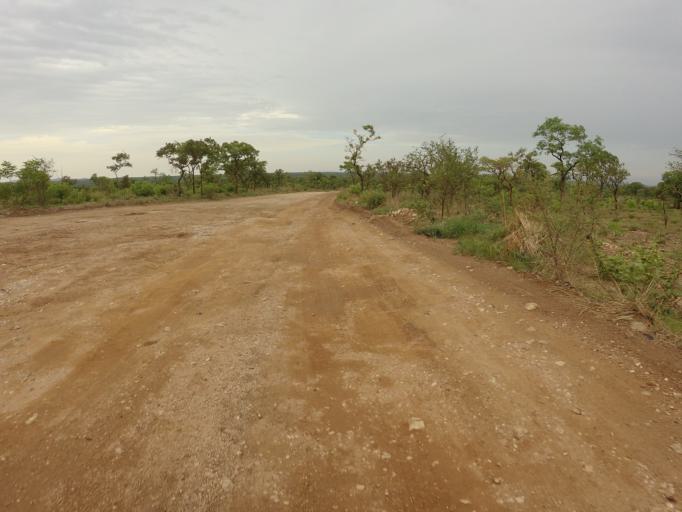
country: GH
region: Upper East
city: Bolgatanga
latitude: 10.8789
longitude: -0.6249
